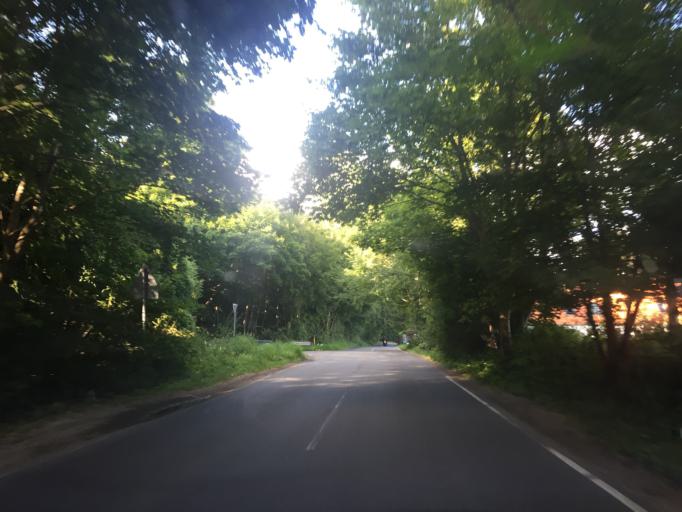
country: DK
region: Capital Region
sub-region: Hoje-Taastrup Kommune
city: Taastrup
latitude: 55.6919
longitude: 12.2460
